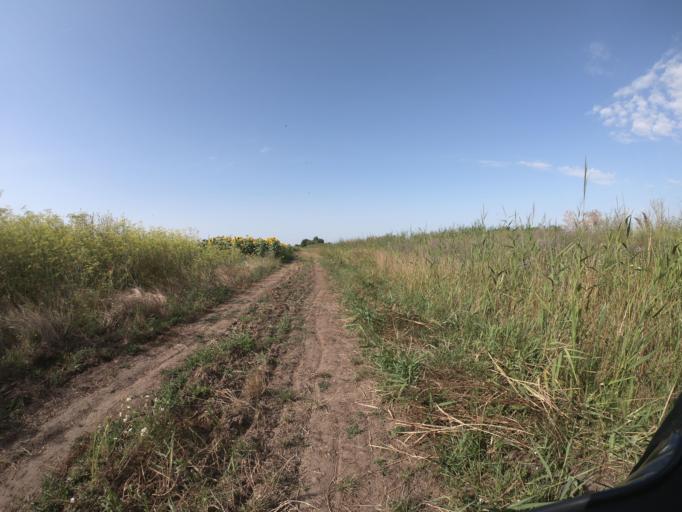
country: HU
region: Hajdu-Bihar
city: Egyek
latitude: 47.5869
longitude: 20.9628
